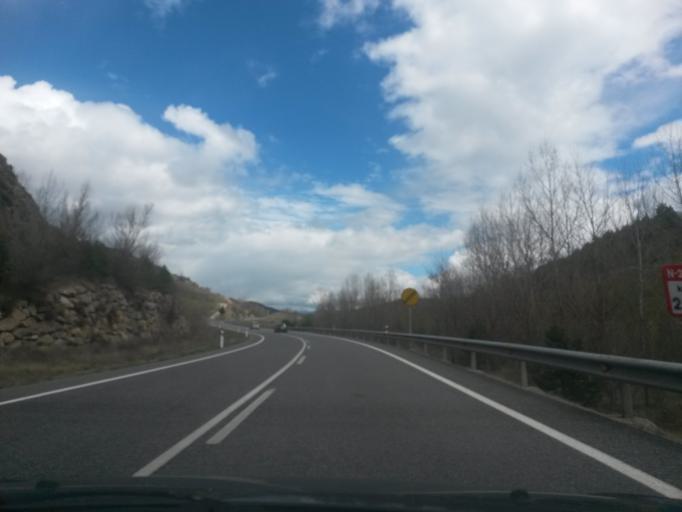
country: ES
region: Catalonia
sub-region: Provincia de Lleida
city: Lles de Cerdanya
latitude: 42.3653
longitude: 1.7154
